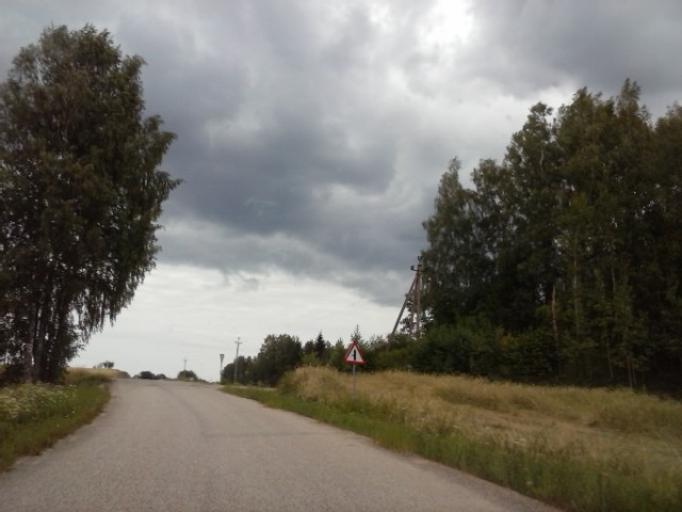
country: EE
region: Vorumaa
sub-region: Voru linn
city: Voru
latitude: 57.7415
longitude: 27.1104
